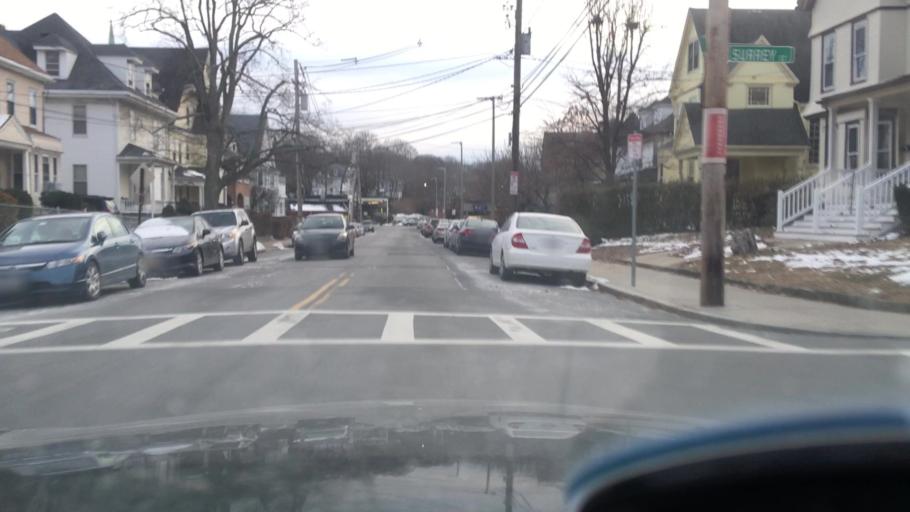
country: US
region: Massachusetts
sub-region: Middlesex County
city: Watertown
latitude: 42.3506
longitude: -71.1553
